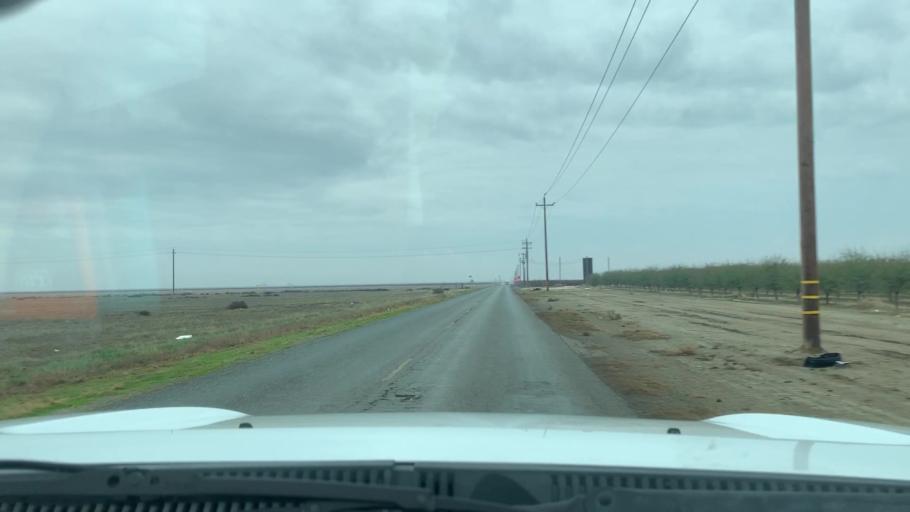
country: US
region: California
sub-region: Tulare County
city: Alpaugh
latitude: 35.7611
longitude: -119.4035
